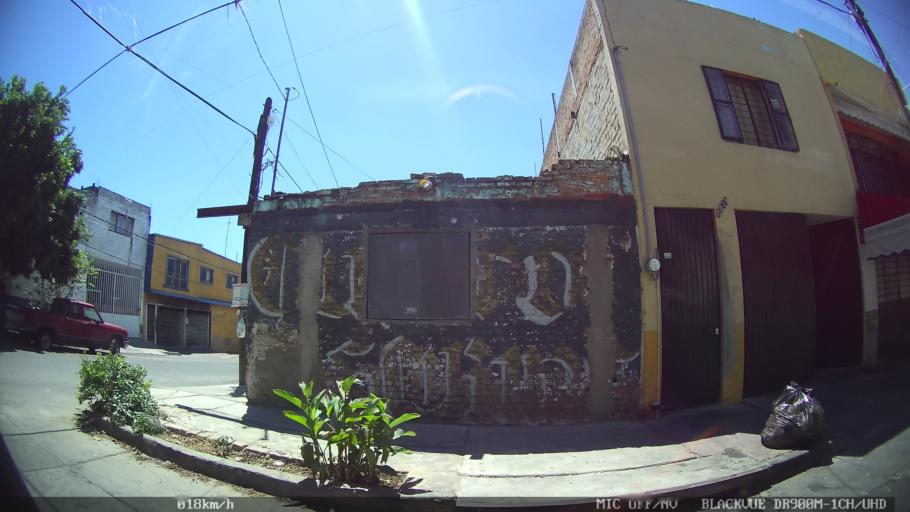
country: MX
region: Jalisco
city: Tlaquepaque
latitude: 20.6868
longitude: -103.2927
